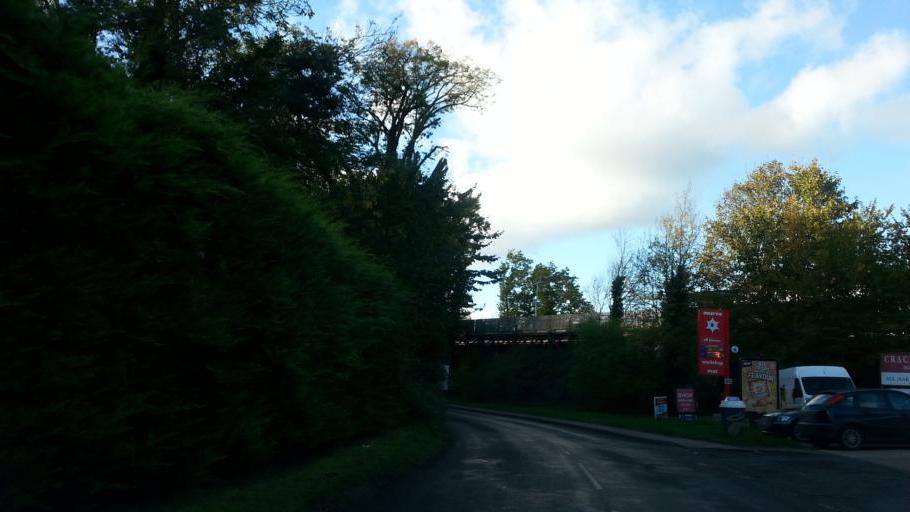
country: GB
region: England
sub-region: Suffolk
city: Thurston
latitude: 52.2494
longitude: 0.8092
